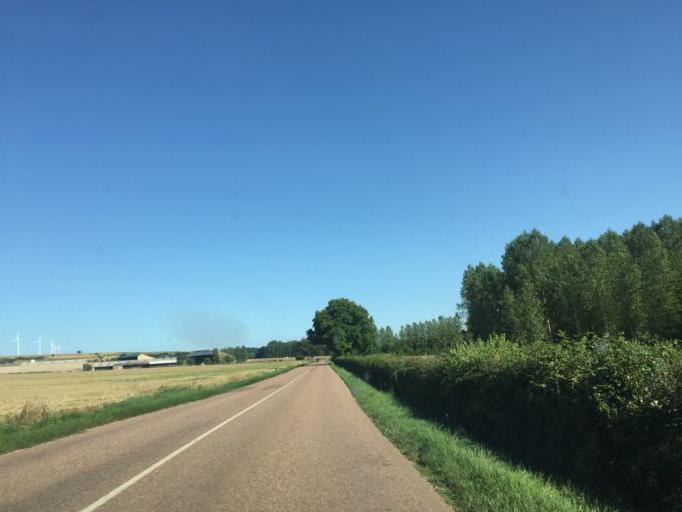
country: FR
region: Bourgogne
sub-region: Departement de l'Yonne
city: Fontenailles
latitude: 47.4801
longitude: 3.4258
